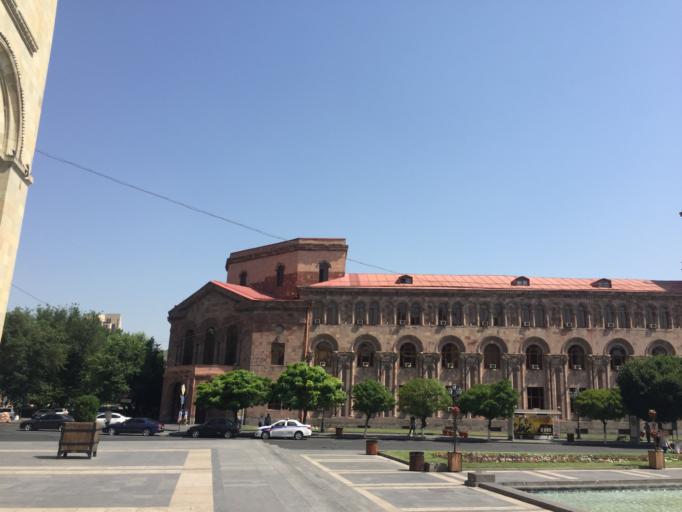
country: AM
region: Yerevan
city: Yerevan
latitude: 40.1784
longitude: 44.5139
